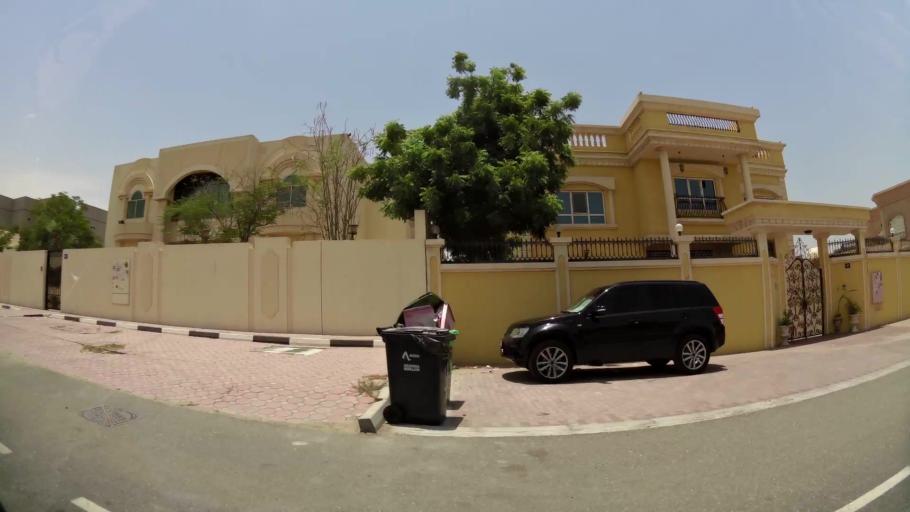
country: AE
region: Ash Shariqah
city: Sharjah
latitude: 25.2106
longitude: 55.3773
